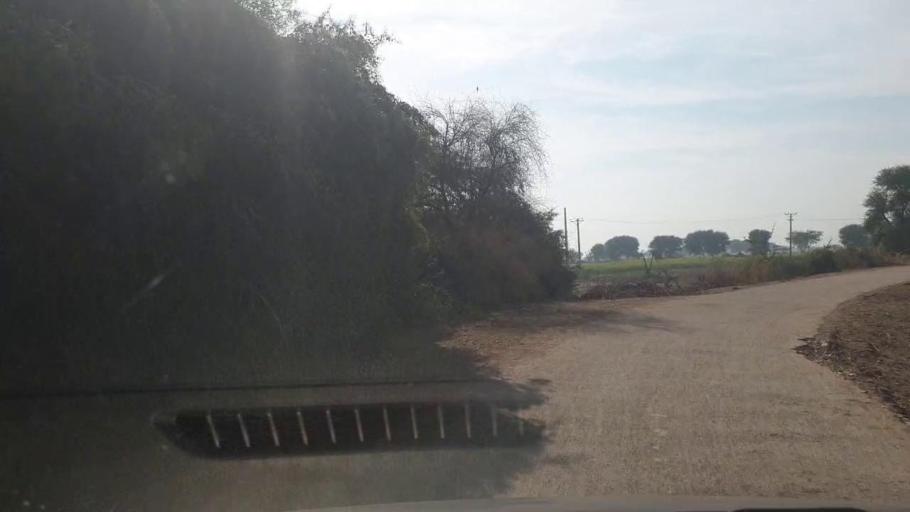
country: PK
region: Sindh
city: Shahpur Chakar
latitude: 26.1835
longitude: 68.5853
